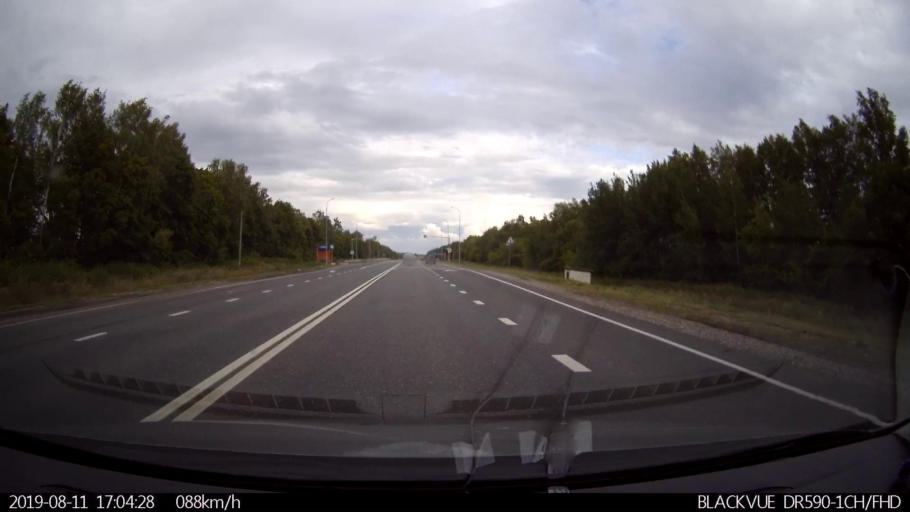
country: RU
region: Ulyanovsk
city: Mayna
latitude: 54.3006
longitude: 47.7648
